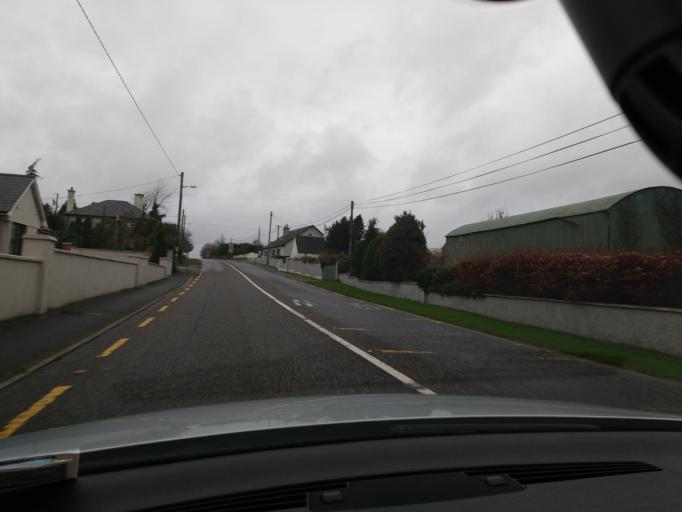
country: IE
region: Munster
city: Thurles
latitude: 52.6722
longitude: -7.6966
